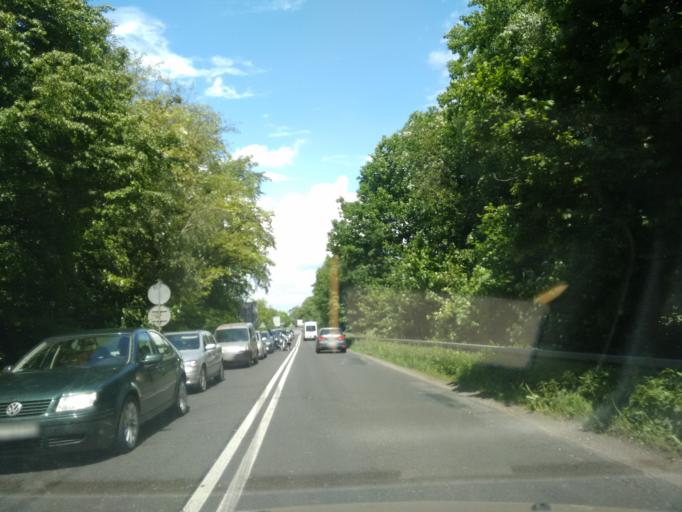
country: PL
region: Silesian Voivodeship
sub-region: Powiat cieszynski
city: Pruchna
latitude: 49.8663
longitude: 18.6825
